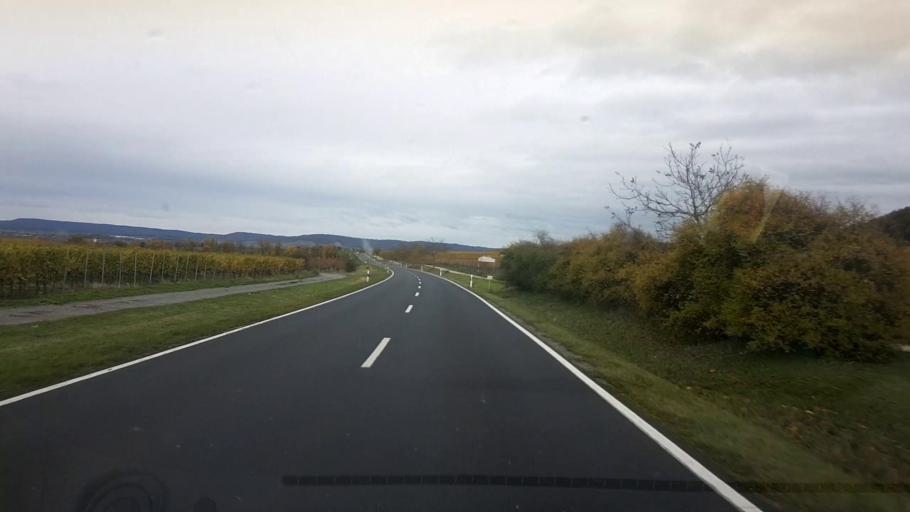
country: DE
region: Bavaria
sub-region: Regierungsbezirk Unterfranken
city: Rodelsee
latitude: 49.7350
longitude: 10.2757
